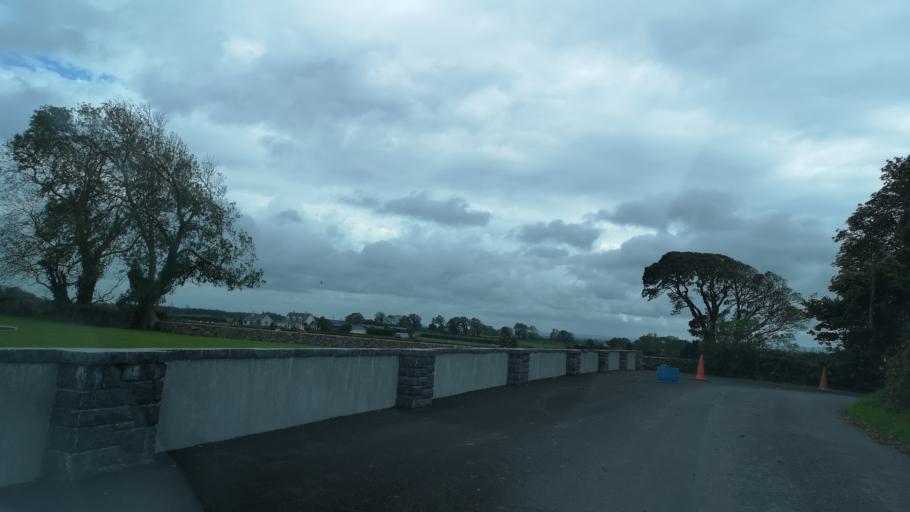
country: IE
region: Connaught
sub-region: County Galway
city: Athenry
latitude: 53.2974
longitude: -8.6821
